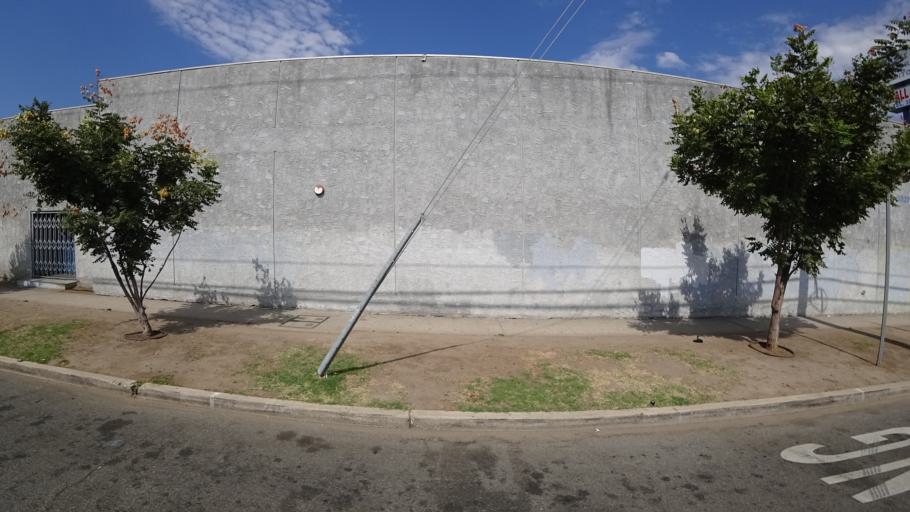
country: US
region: California
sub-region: Los Angeles County
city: Westmont
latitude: 33.9550
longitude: -118.2828
